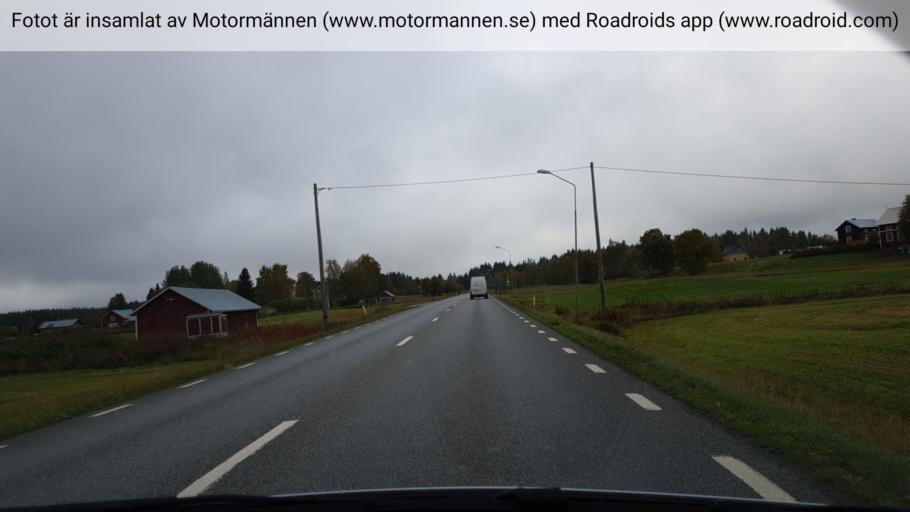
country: SE
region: Jaemtland
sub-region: Stroemsunds Kommun
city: Stroemsund
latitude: 63.4953
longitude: 15.2533
